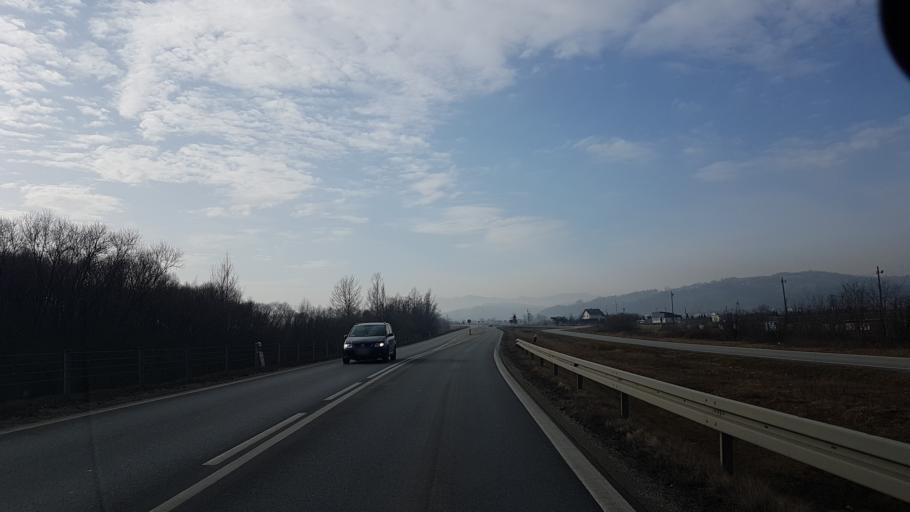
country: PL
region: Lesser Poland Voivodeship
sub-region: Powiat nowosadecki
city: Podegrodzie
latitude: 49.5738
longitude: 20.6058
